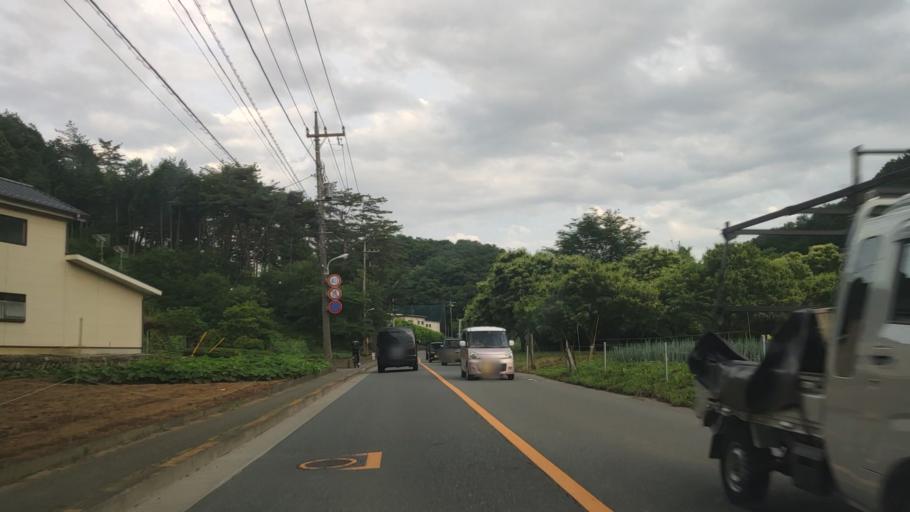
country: JP
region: Saitama
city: Hanno
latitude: 35.8173
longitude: 139.2965
